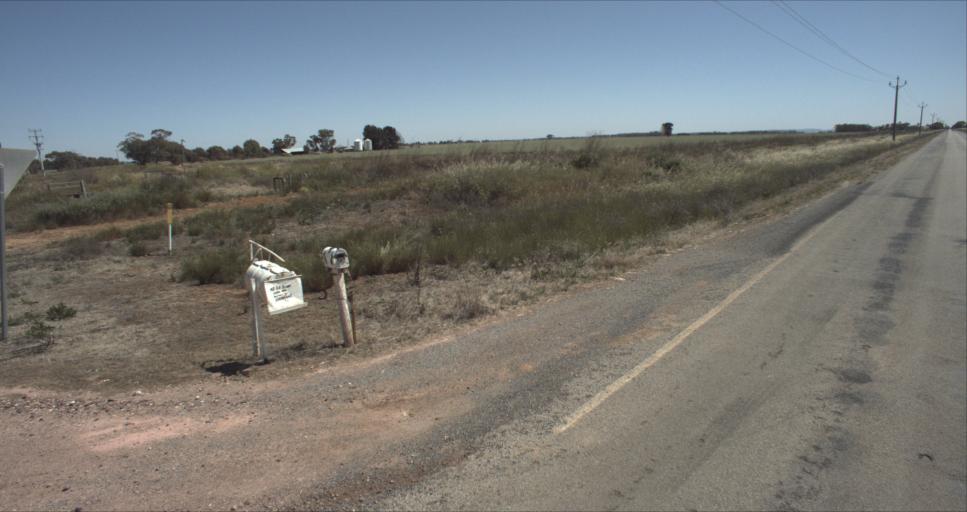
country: AU
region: New South Wales
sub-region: Leeton
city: Leeton
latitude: -34.5136
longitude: 146.2846
